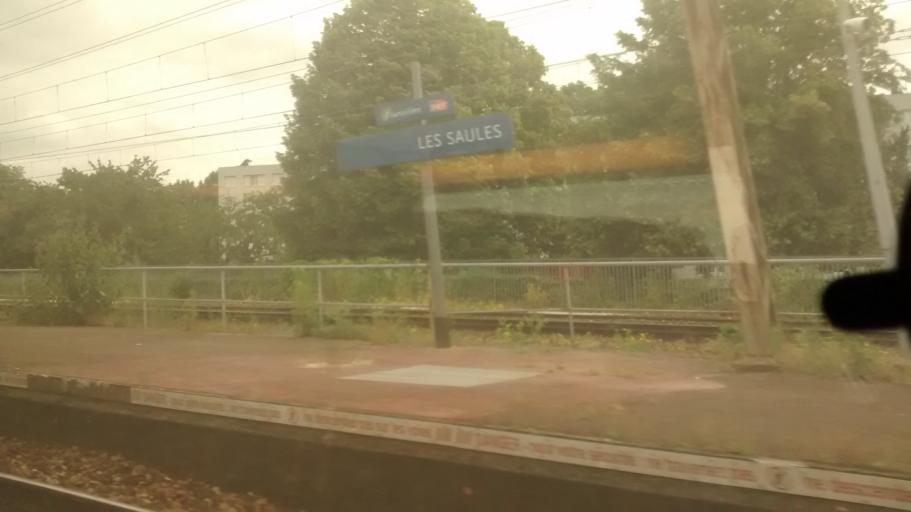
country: FR
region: Ile-de-France
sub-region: Departement du Val-de-Marne
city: Villeneuve-le-Roi
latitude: 48.7445
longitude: 2.4174
